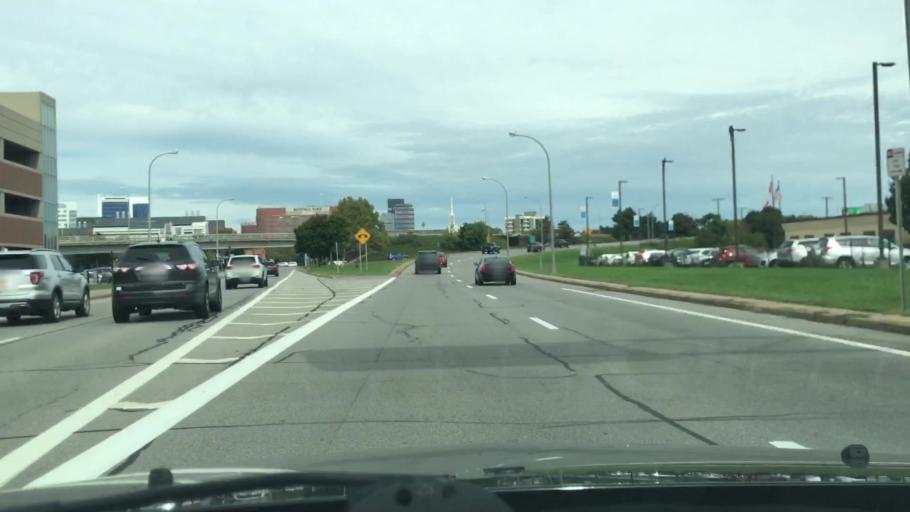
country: US
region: New York
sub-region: Erie County
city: Buffalo
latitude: 42.8914
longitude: -78.8673
